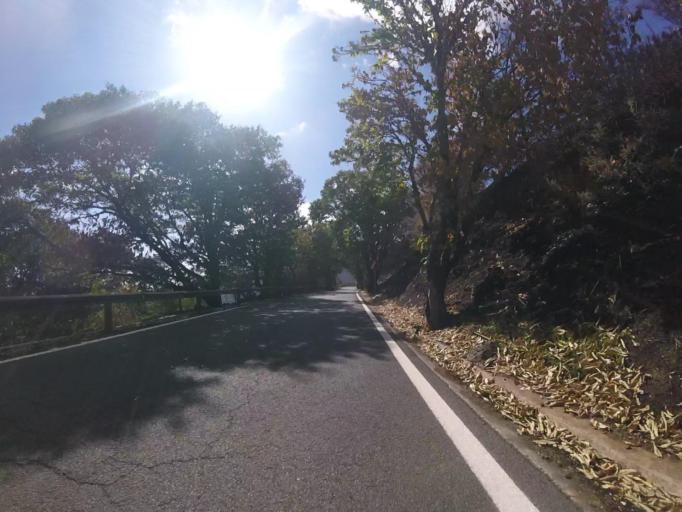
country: ES
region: Canary Islands
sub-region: Provincia de Las Palmas
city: Valleseco
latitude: 28.0110
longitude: -15.5847
